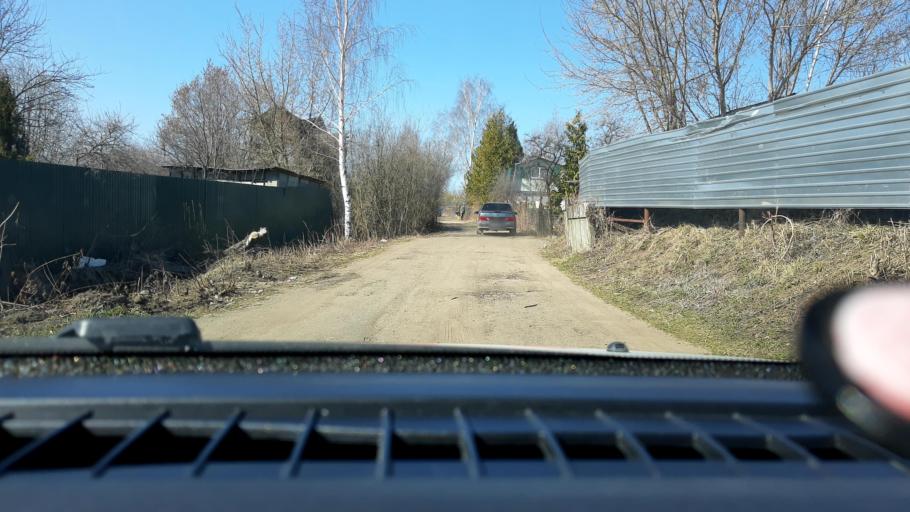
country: RU
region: Nizjnij Novgorod
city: Gorbatovka
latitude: 56.2627
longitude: 43.8241
